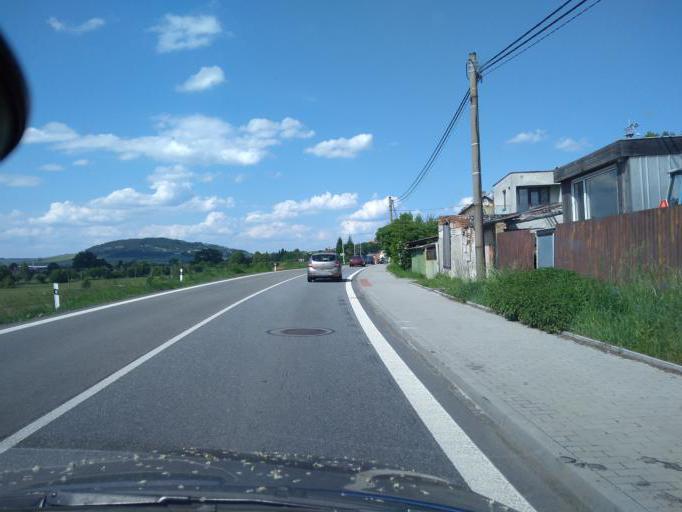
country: CZ
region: Plzensky
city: Svihov
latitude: 49.4734
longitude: 13.2896
